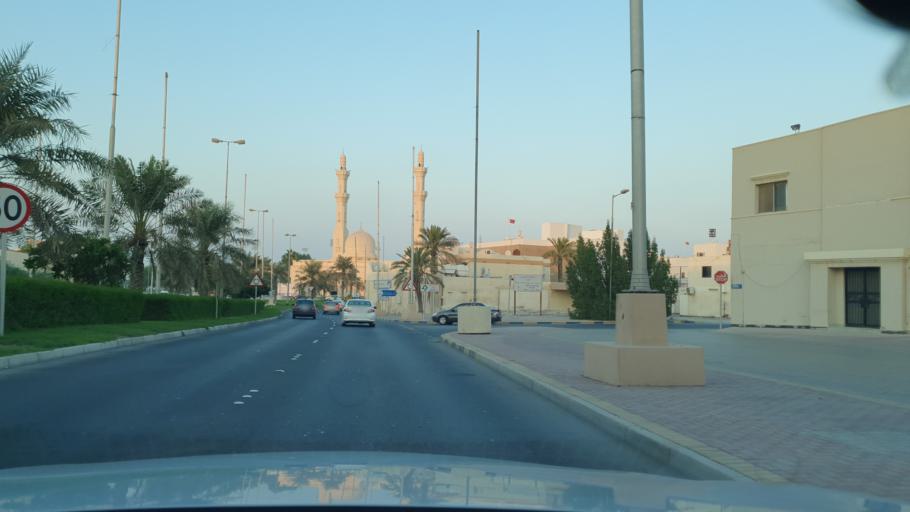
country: BH
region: Northern
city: Madinat `Isa
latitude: 26.1698
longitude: 50.5450
